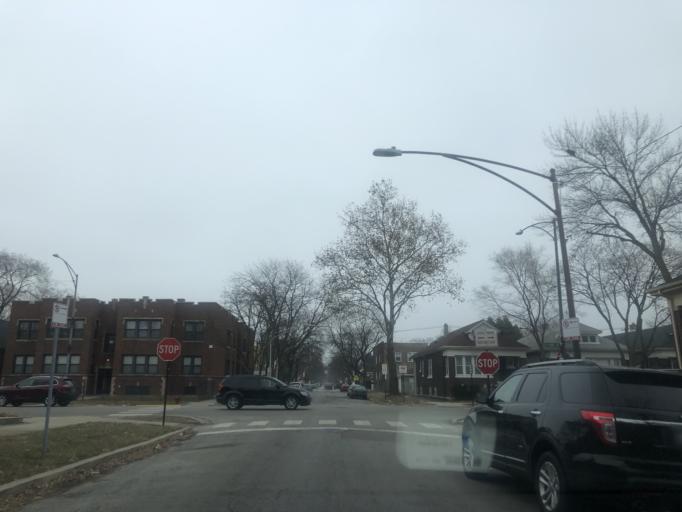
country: US
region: Illinois
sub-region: Cook County
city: Evergreen Park
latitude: 41.7529
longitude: -87.6155
